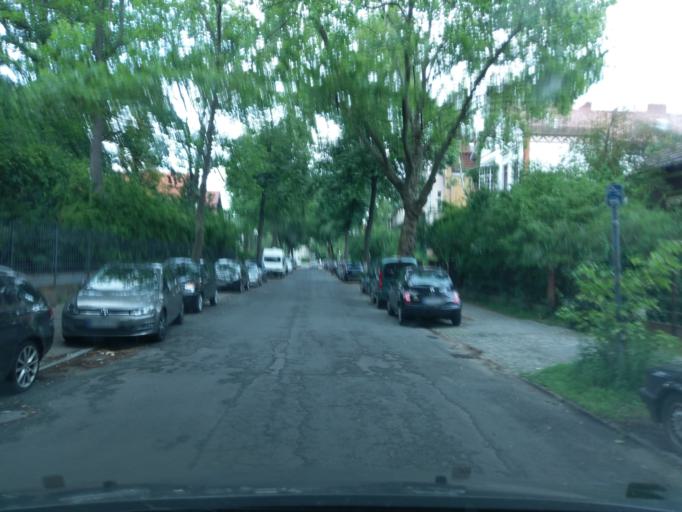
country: DE
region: Berlin
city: Lichterfelde
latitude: 52.4435
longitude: 13.3080
